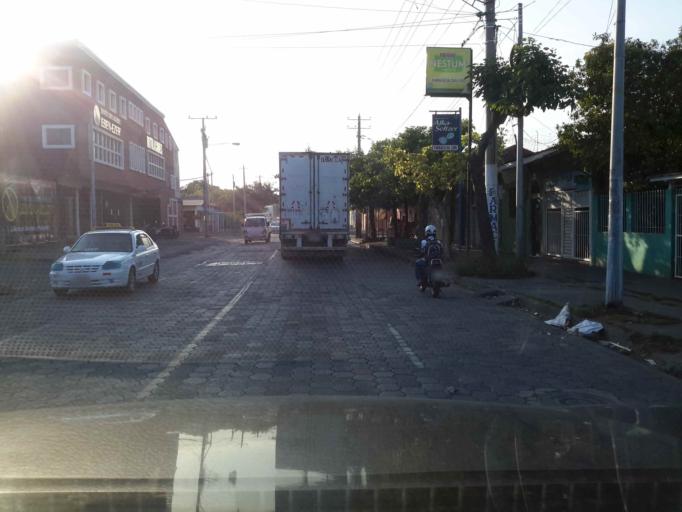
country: NI
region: Managua
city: Managua
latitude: 12.1578
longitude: -86.2926
